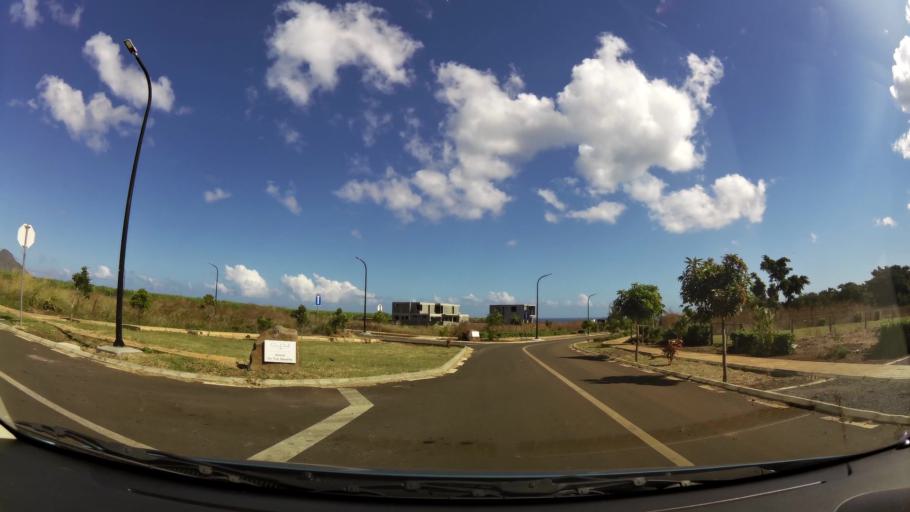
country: MU
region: Black River
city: Cascavelle
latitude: -20.2827
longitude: 57.3877
